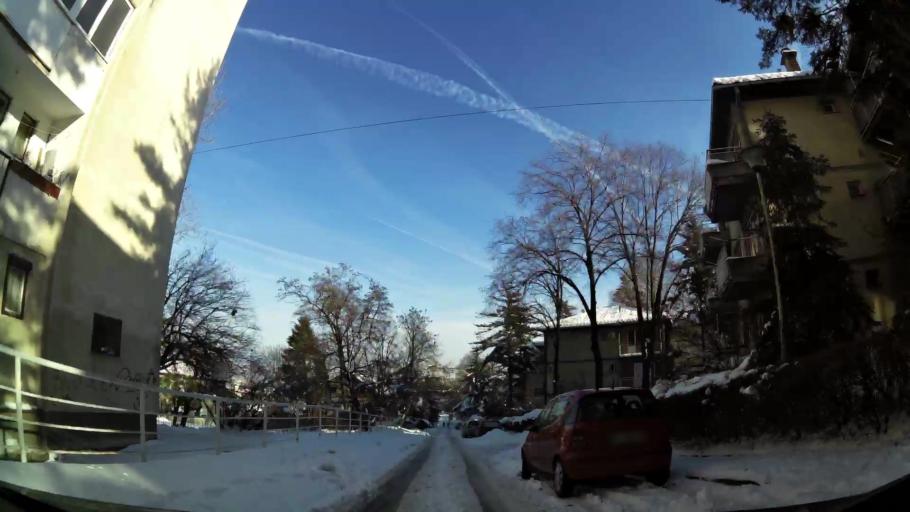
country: RS
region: Central Serbia
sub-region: Belgrade
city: Palilula
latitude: 44.8139
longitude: 20.5025
